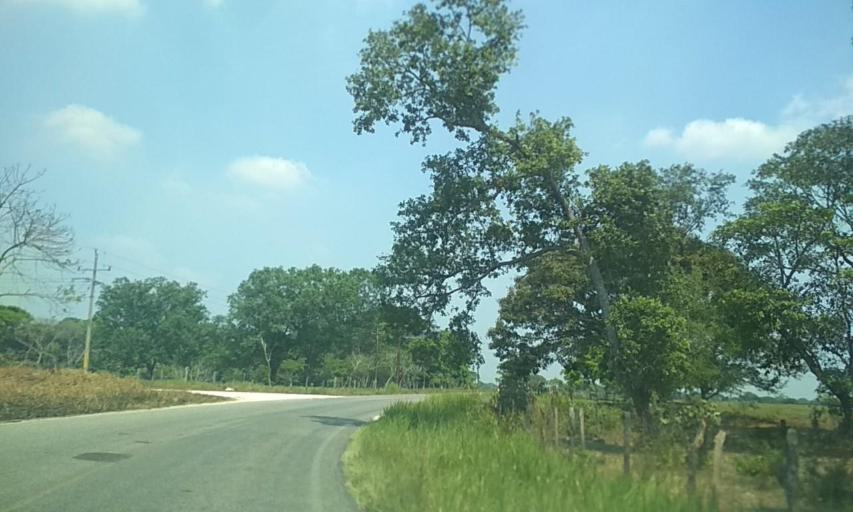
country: MX
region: Tabasco
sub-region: Cardenas
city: Poblado C-33 20 de Noviembre
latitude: 17.8528
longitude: -93.5772
